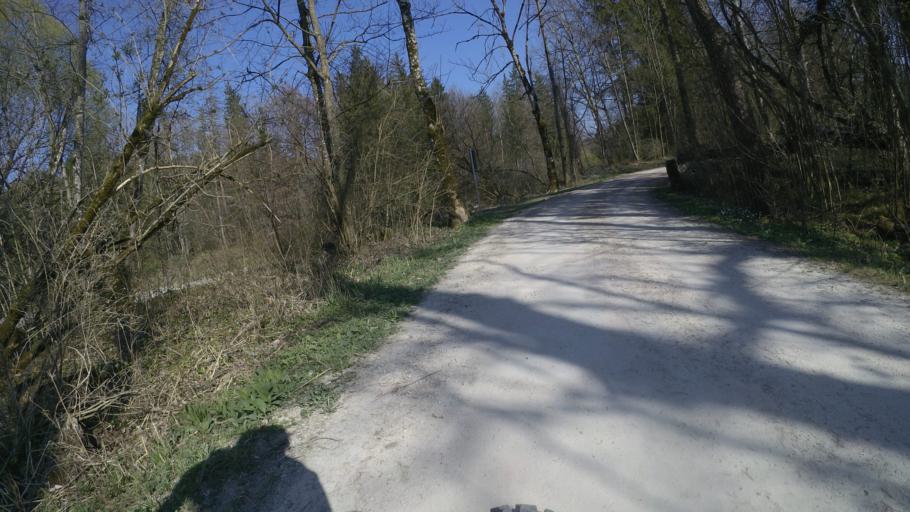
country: DE
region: Bavaria
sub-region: Upper Bavaria
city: Traunreut
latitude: 47.9581
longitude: 12.5762
